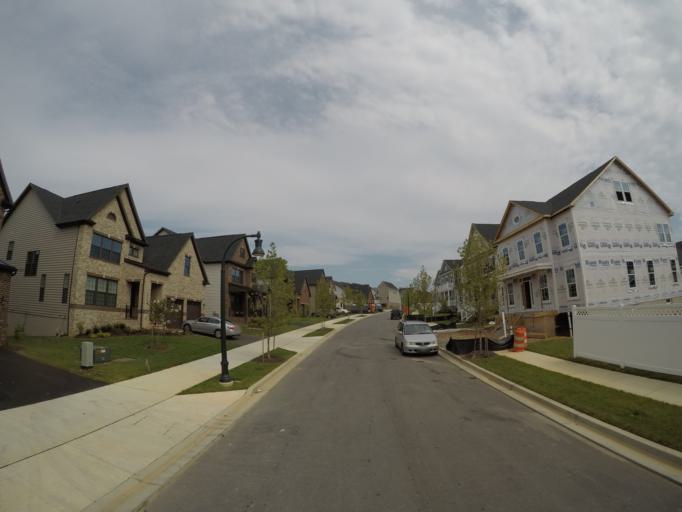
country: US
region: Maryland
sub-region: Montgomery County
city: Clarksburg
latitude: 39.2166
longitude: -77.2884
